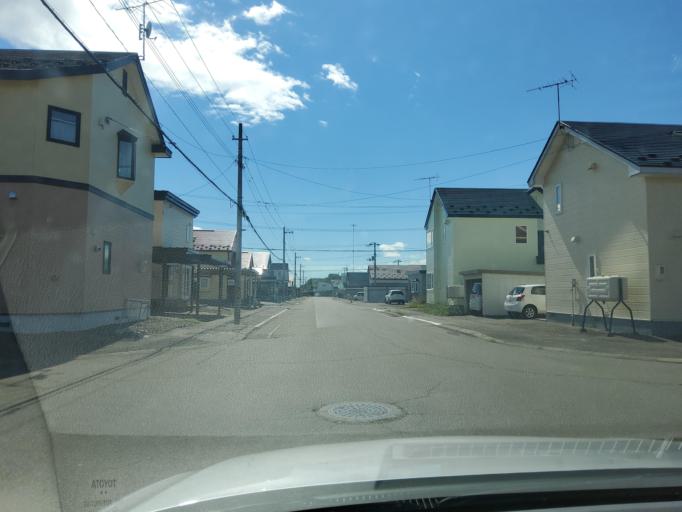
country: JP
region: Hokkaido
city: Otofuke
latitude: 42.9612
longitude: 143.1959
